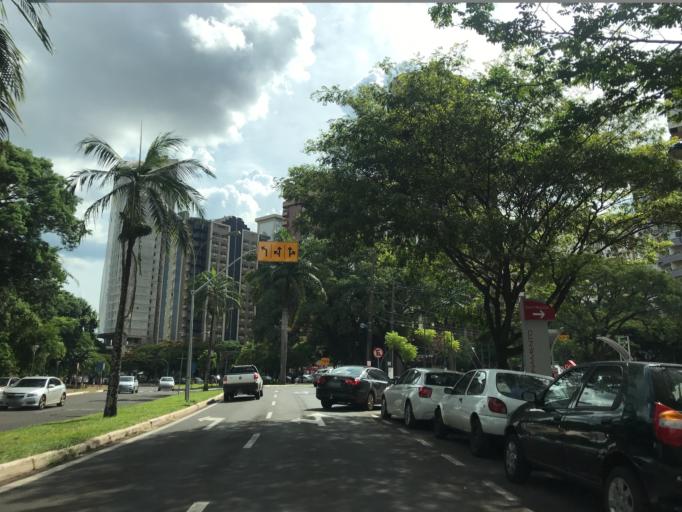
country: BR
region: Parana
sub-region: Maringa
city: Maringa
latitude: -23.4234
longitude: -51.9321
